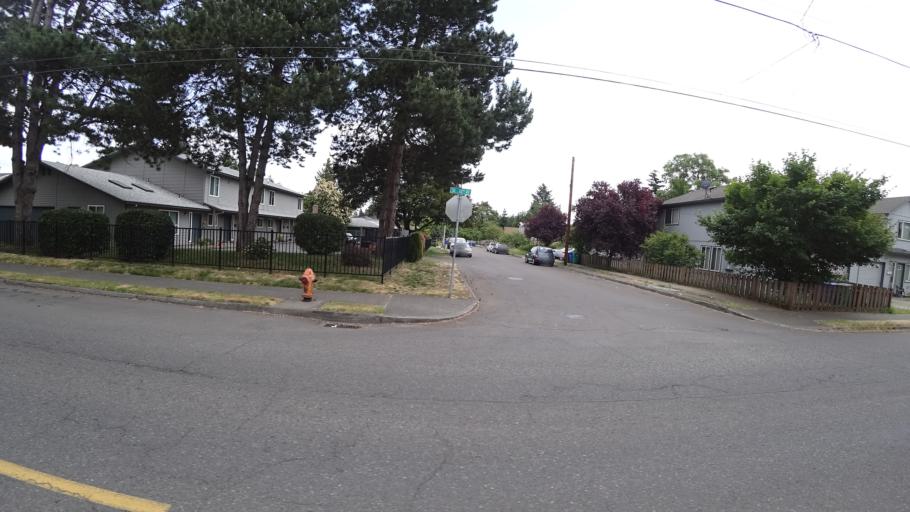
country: US
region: Oregon
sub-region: Multnomah County
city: Lents
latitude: 45.4724
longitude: -122.5894
